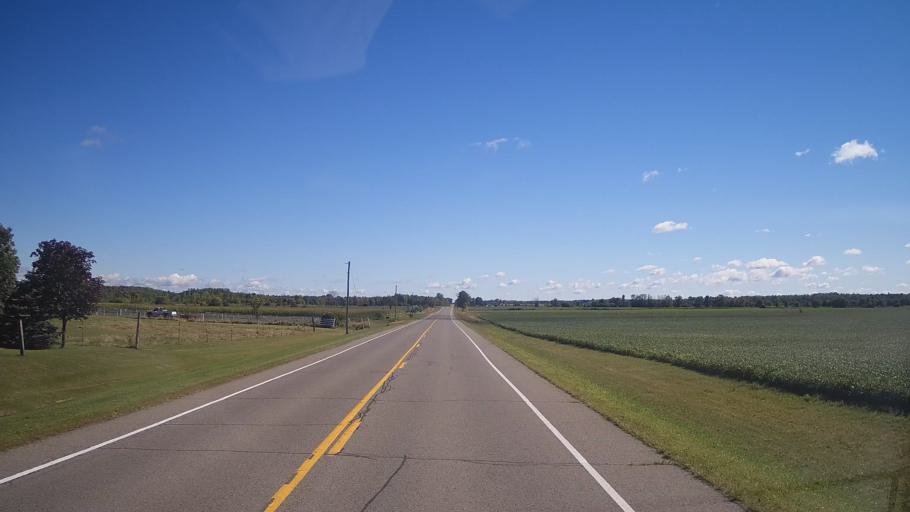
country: CA
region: Ontario
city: Prescott
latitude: 44.9256
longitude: -75.3430
